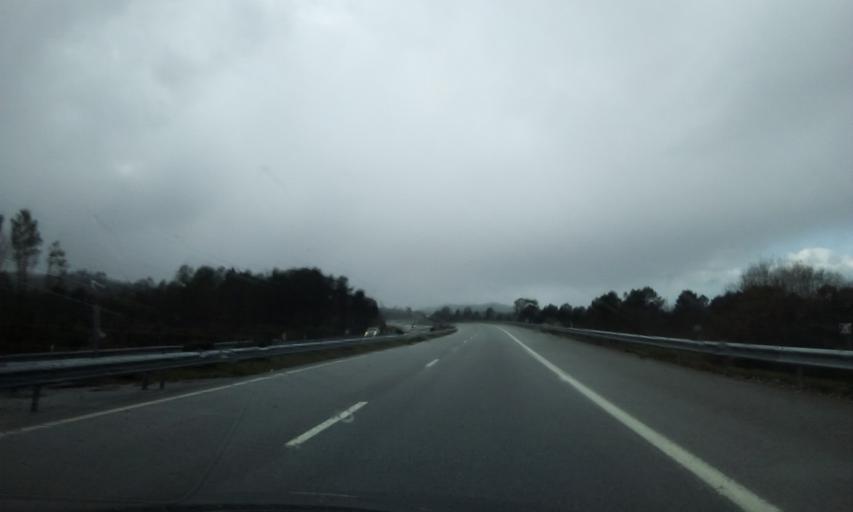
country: PT
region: Viseu
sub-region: Mangualde
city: Mangualde
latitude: 40.6142
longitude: -7.6847
